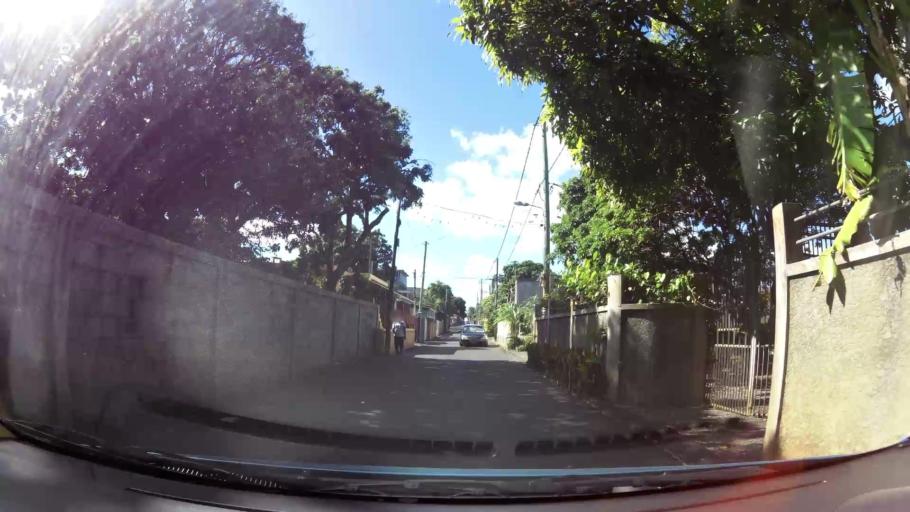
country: MU
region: Plaines Wilhems
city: Vacoas
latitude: -20.2919
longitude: 57.4799
